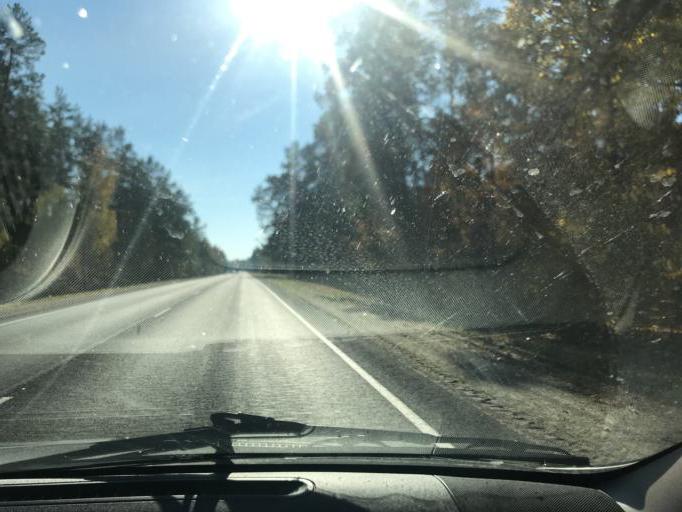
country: BY
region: Brest
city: Mikashevichy
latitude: 52.2595
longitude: 27.4406
